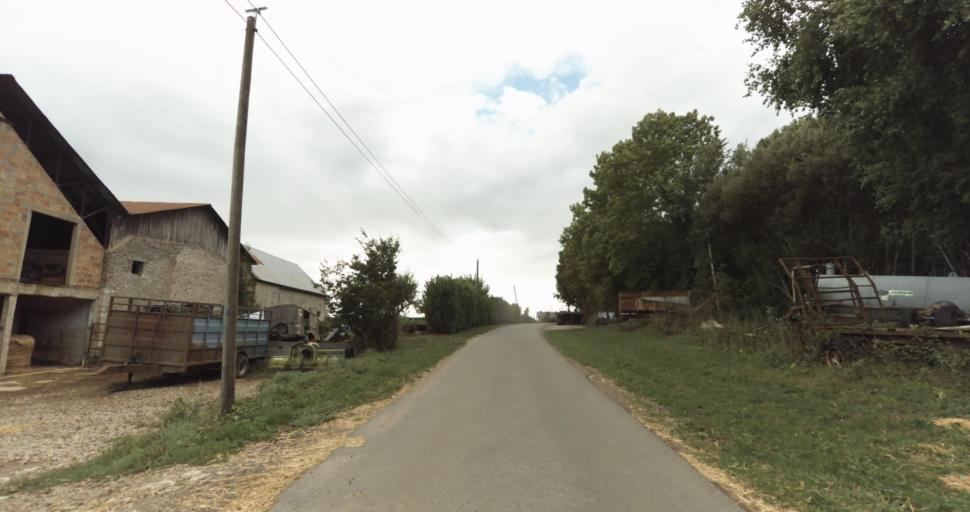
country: FR
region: Lower Normandy
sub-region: Departement de l'Orne
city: Sainte-Gauburge-Sainte-Colombe
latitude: 48.7264
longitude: 0.3962
